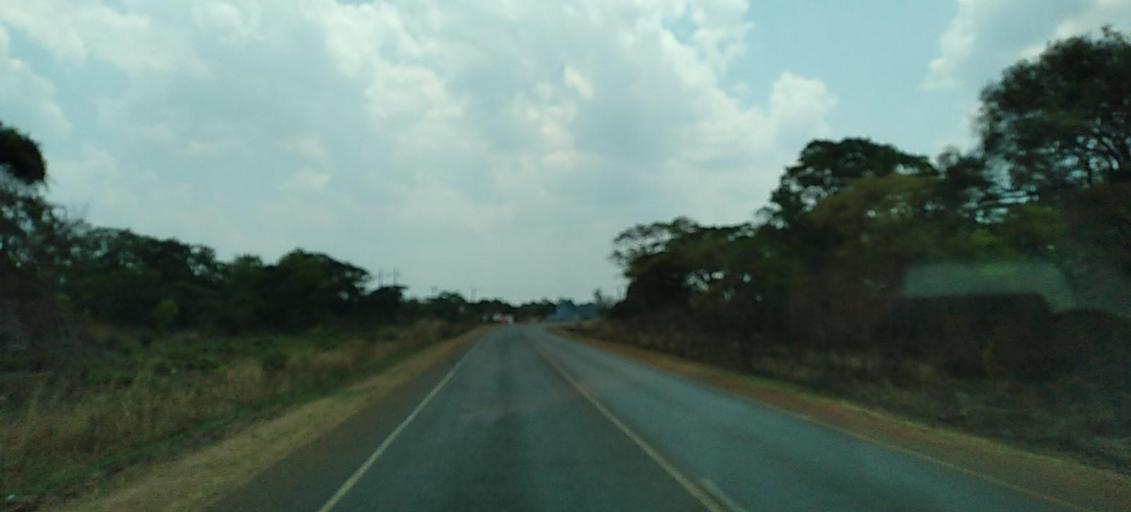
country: ZM
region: Copperbelt
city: Kalulushi
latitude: -12.8445
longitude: 28.0156
